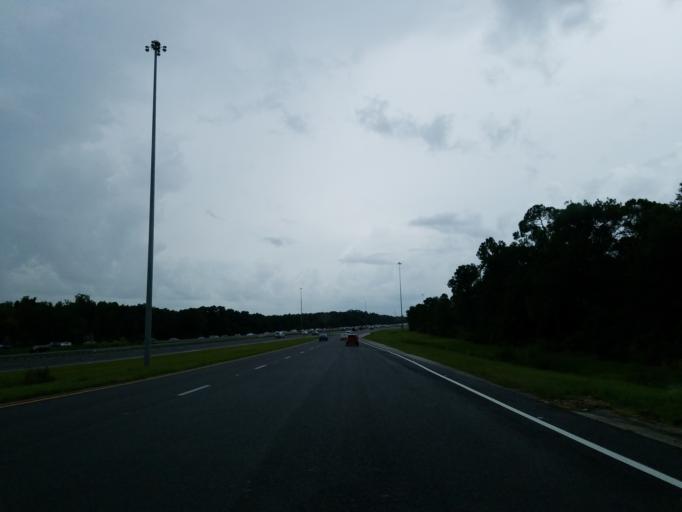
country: US
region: Florida
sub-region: Hillsborough County
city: Pebble Creek
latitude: 28.1930
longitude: -82.3856
